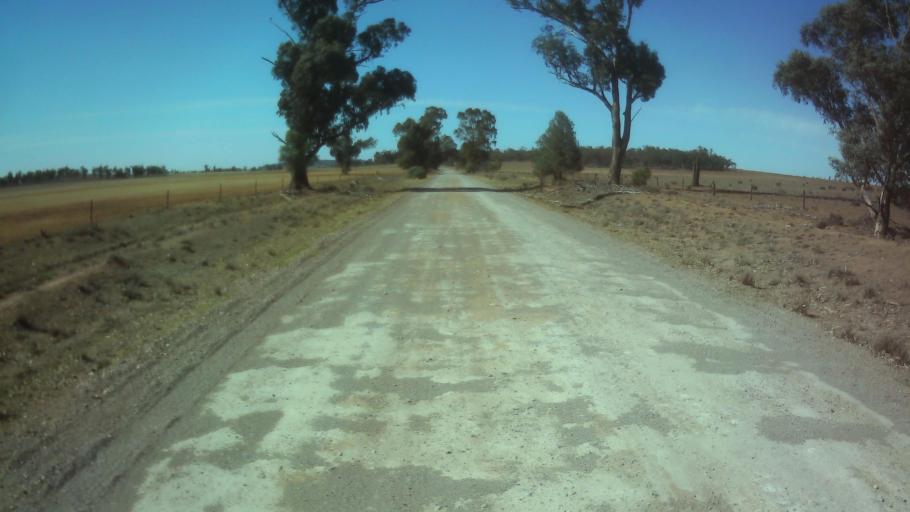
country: AU
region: New South Wales
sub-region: Forbes
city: Forbes
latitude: -33.7196
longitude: 147.7459
